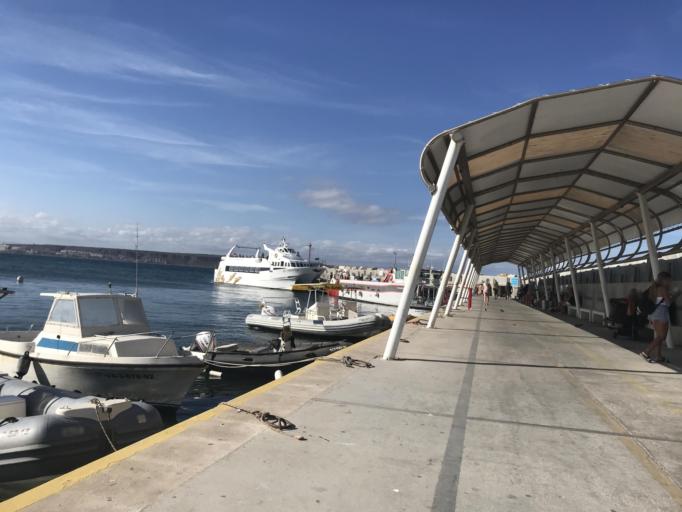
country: ES
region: Valencia
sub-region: Provincia de Alicante
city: Santa Pola
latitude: 38.1668
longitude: -0.4780
